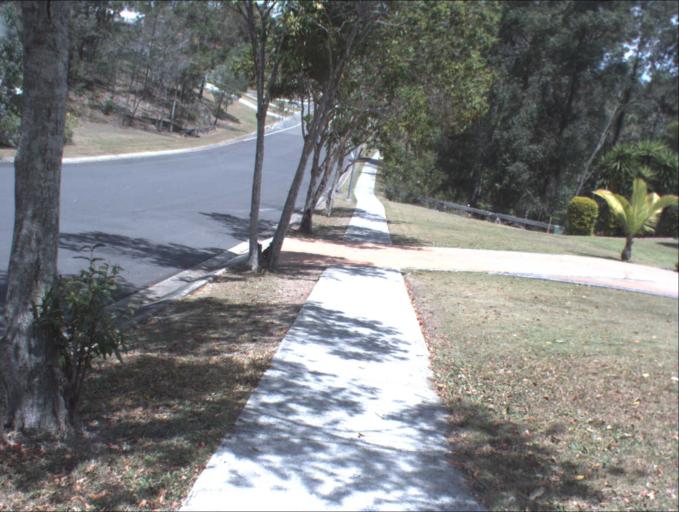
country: AU
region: Queensland
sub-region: Logan
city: Slacks Creek
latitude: -27.6397
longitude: 153.1743
